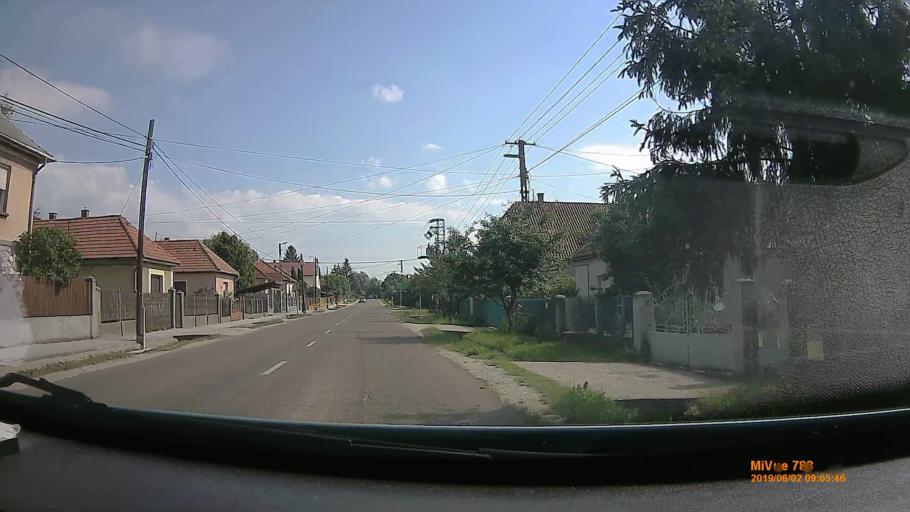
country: HU
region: Borsod-Abauj-Zemplen
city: Kazincbarcika
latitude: 48.1800
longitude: 20.6509
